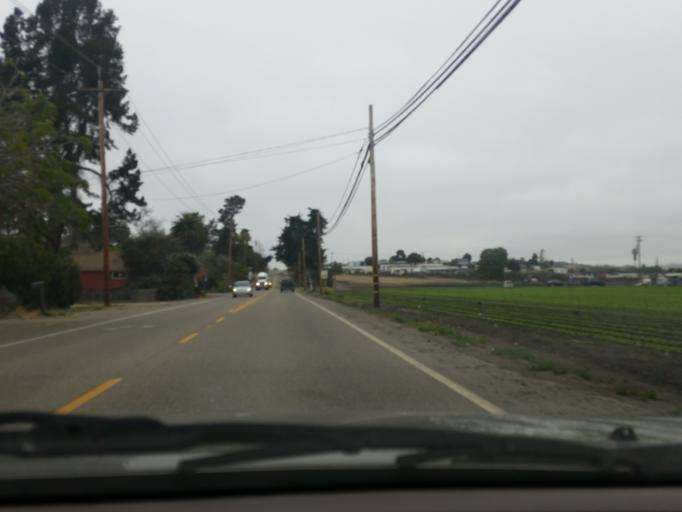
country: US
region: California
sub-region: San Luis Obispo County
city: Arroyo Grande
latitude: 35.1022
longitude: -120.5916
